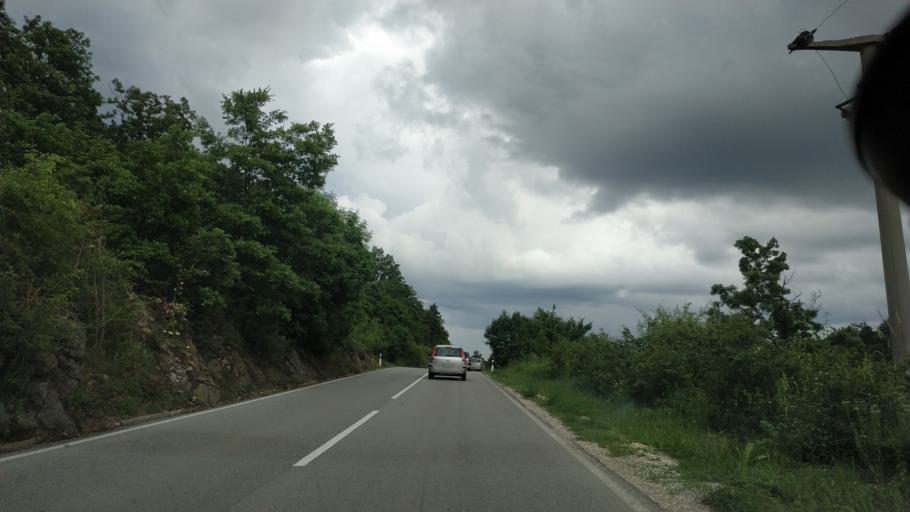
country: RS
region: Central Serbia
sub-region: Borski Okrug
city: Bor
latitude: 44.0495
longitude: 22.0751
